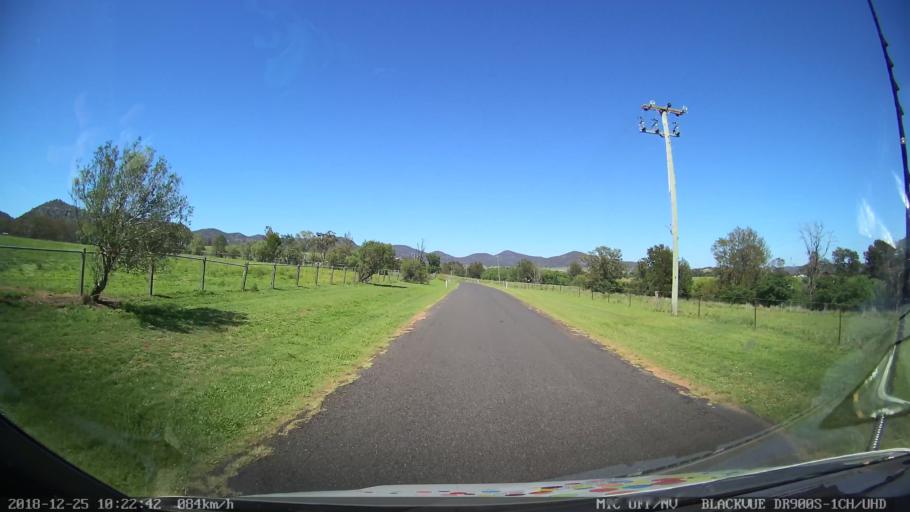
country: AU
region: New South Wales
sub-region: Muswellbrook
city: Denman
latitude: -32.3785
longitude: 150.5294
